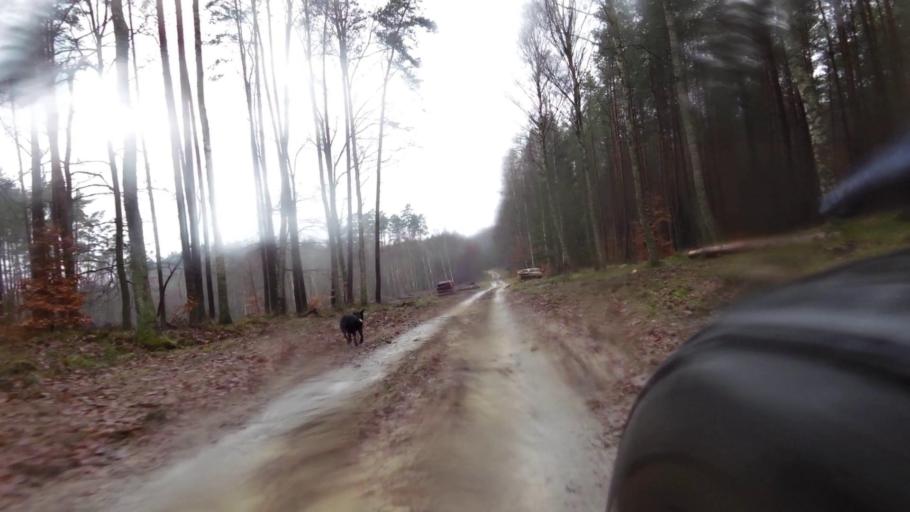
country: PL
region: West Pomeranian Voivodeship
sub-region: Powiat drawski
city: Zlocieniec
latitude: 53.5523
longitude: 15.9377
